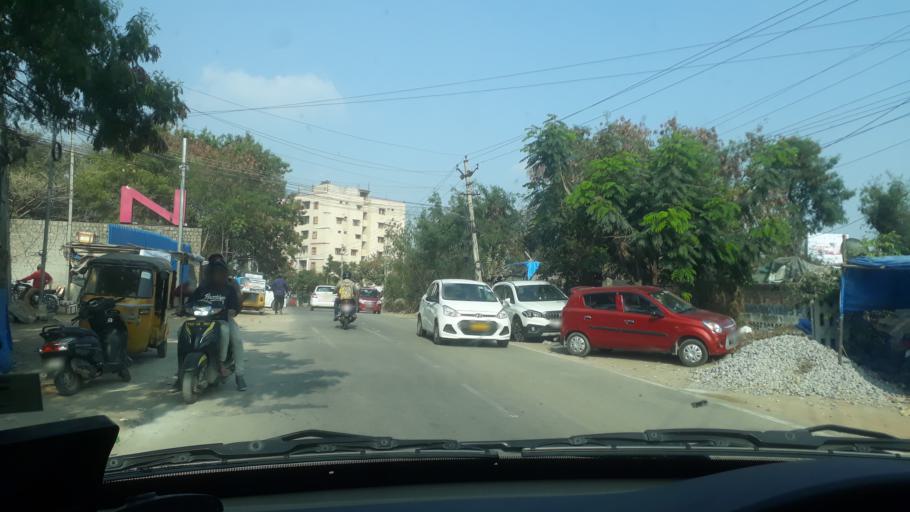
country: IN
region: Telangana
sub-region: Rangareddi
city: Kukatpalli
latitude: 17.4542
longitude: 78.3813
